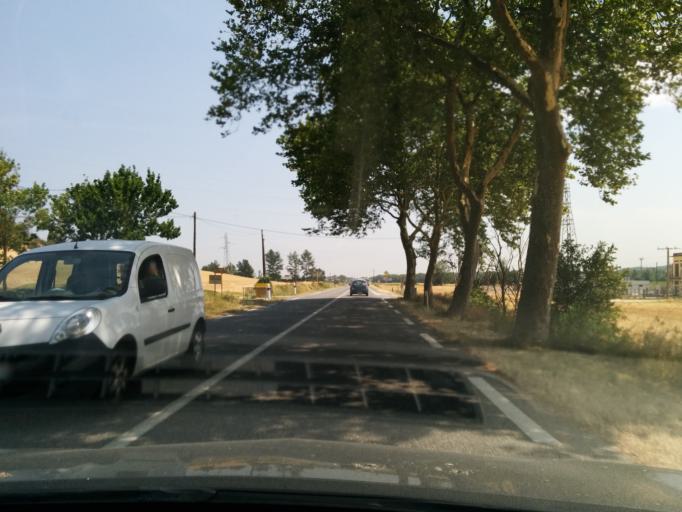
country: FR
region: Midi-Pyrenees
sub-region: Departement de la Haute-Garonne
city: Avignonet-Lauragais
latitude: 43.3640
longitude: 1.7919
